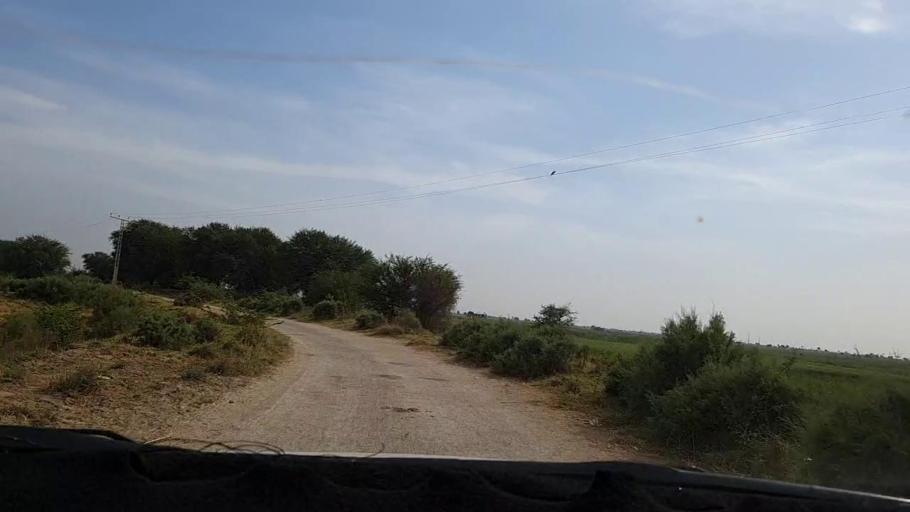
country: PK
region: Sindh
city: Pithoro
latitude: 25.5482
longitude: 69.3292
